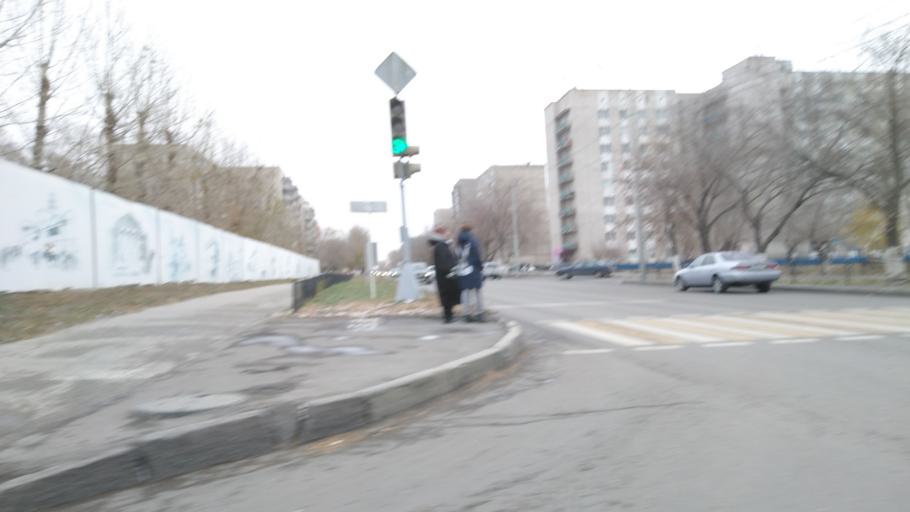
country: KZ
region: Pavlodar
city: Pavlodar
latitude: 52.2757
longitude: 76.9622
